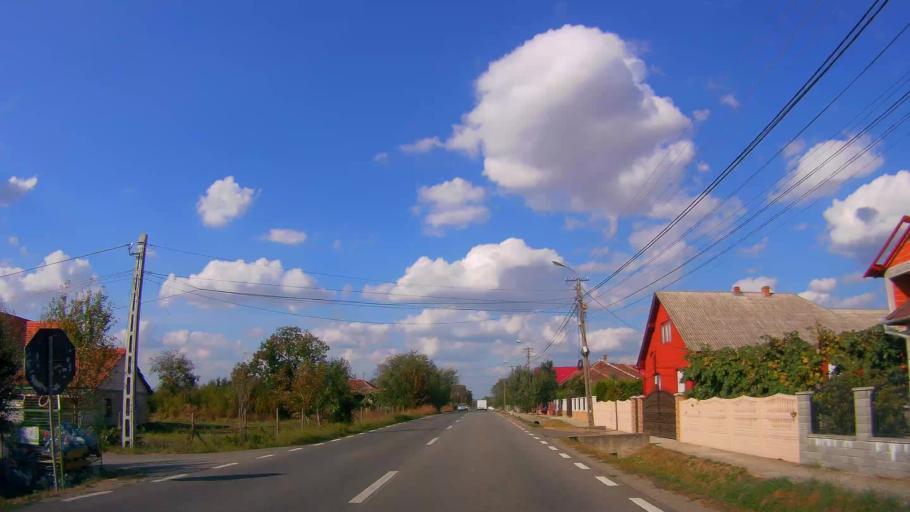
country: RO
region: Satu Mare
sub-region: Comuna Turulung
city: Draguseni
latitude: 47.8956
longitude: 23.0744
